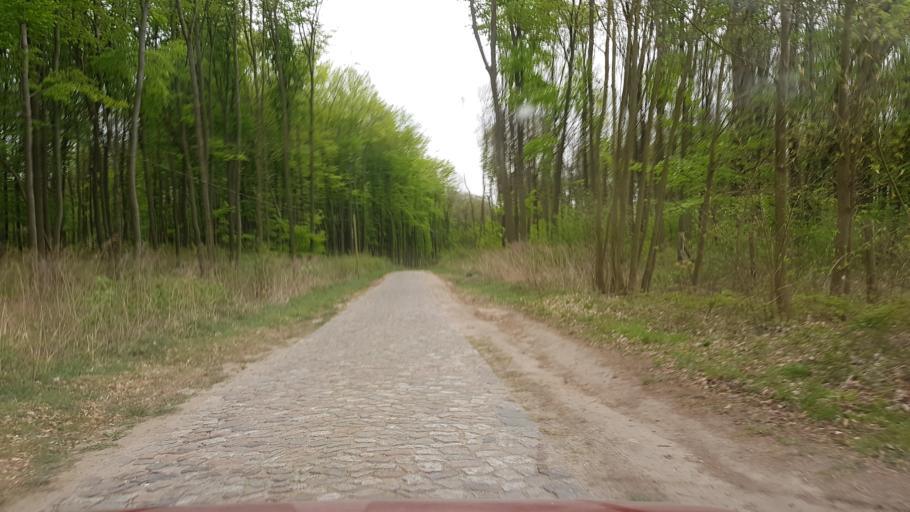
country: PL
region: West Pomeranian Voivodeship
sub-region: Powiat gryfinski
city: Stare Czarnowo
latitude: 53.2938
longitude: 14.7260
